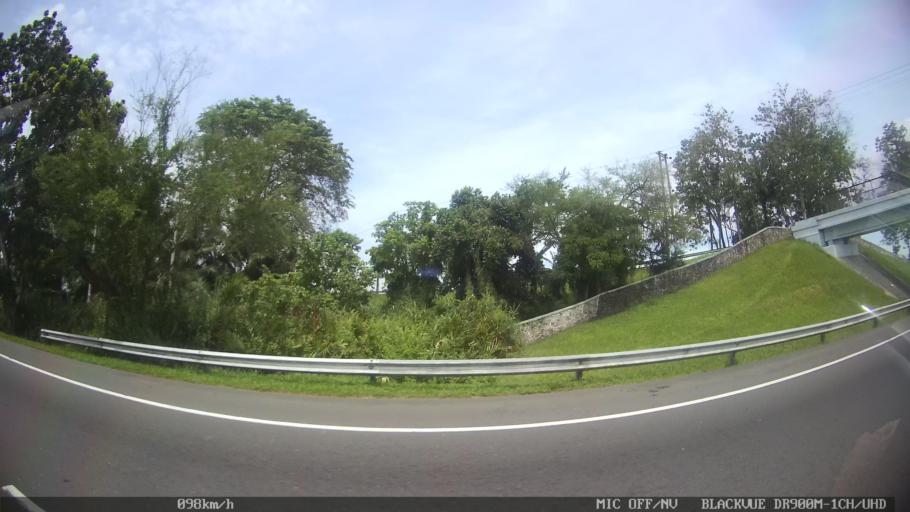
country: ID
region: North Sumatra
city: Labuhan Deli
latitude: 3.7421
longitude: 98.6793
